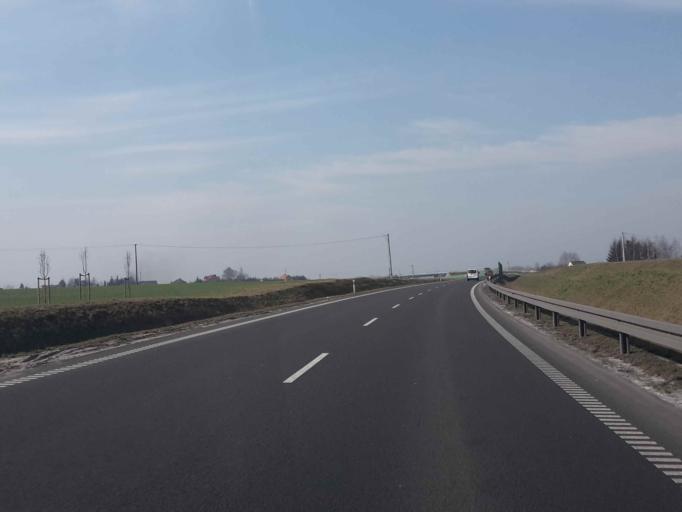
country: PL
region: Kujawsko-Pomorskie
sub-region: Powiat torunski
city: Lubicz Dolny
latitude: 53.0961
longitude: 18.7699
